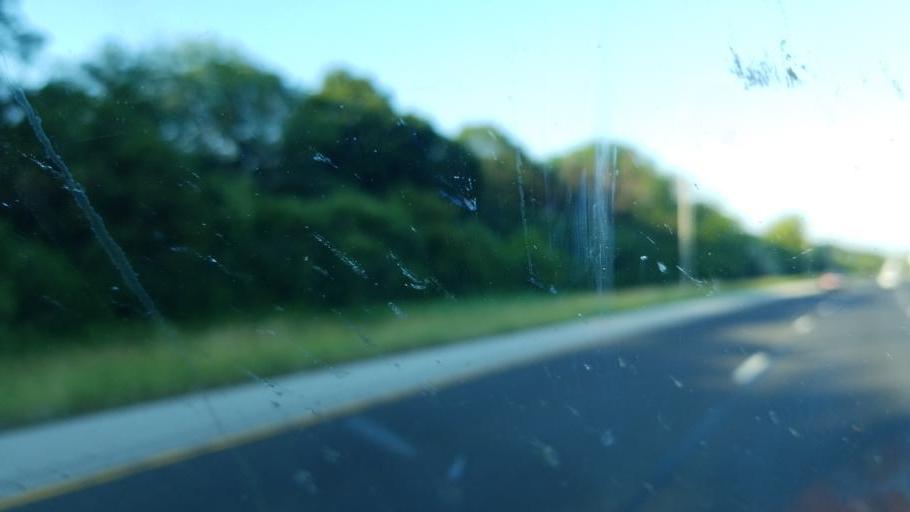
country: US
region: Illinois
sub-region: Cook County
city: Country Club Hills
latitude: 41.5651
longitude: -87.7462
